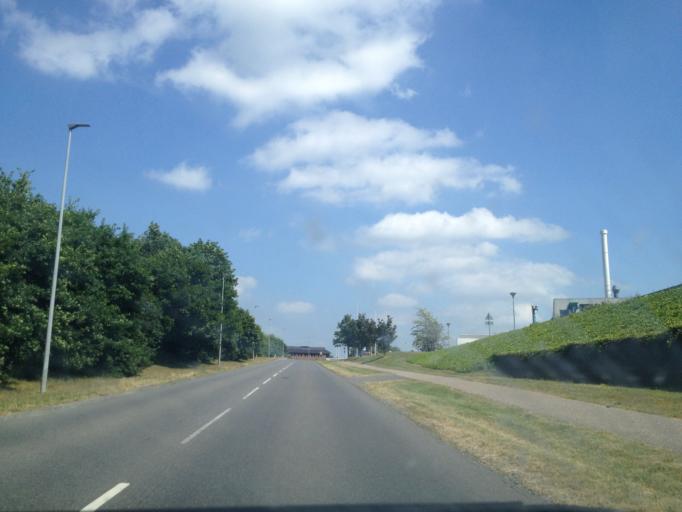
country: DK
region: South Denmark
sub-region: Kolding Kommune
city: Vamdrup
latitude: 55.4370
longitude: 9.2969
